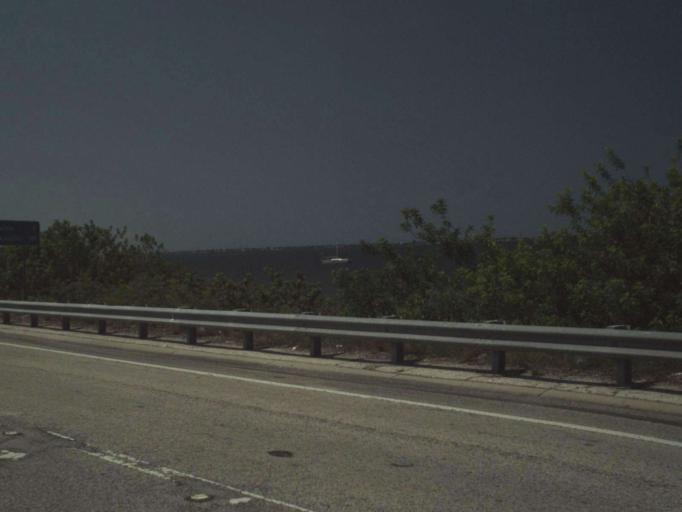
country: US
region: Florida
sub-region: Brevard County
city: Malabar
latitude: 28.0046
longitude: -80.5638
